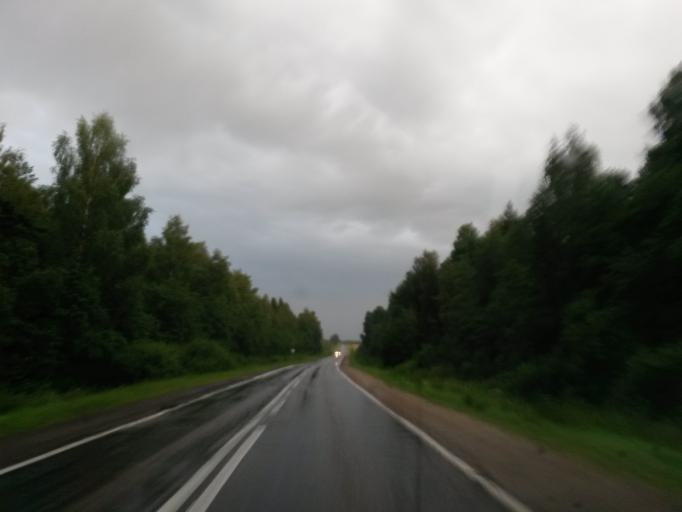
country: RU
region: Jaroslavl
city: Krasnyye Tkachi
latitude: 57.4713
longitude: 39.9085
